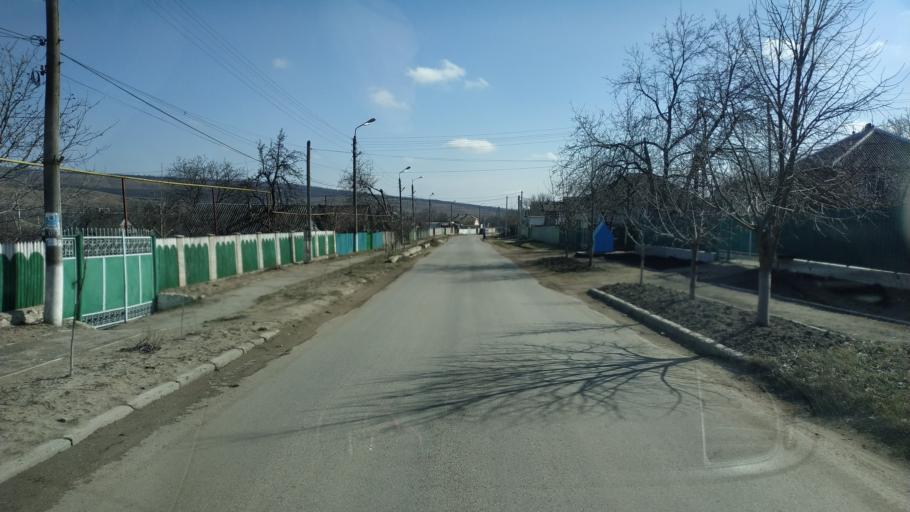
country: MD
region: Hincesti
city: Hincesti
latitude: 46.9667
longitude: 28.5952
